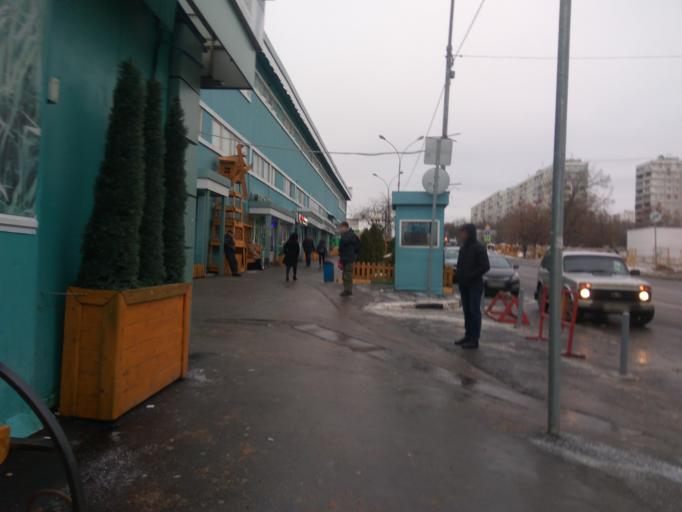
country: RU
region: Moscow
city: Orekhovo-Borisovo
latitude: 55.6103
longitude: 37.7225
